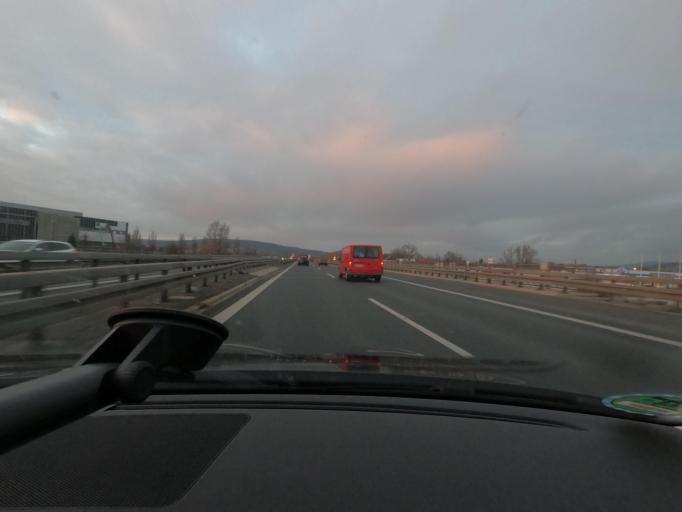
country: DE
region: Bavaria
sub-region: Upper Franconia
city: Forchheim
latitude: 49.7054
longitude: 11.0583
